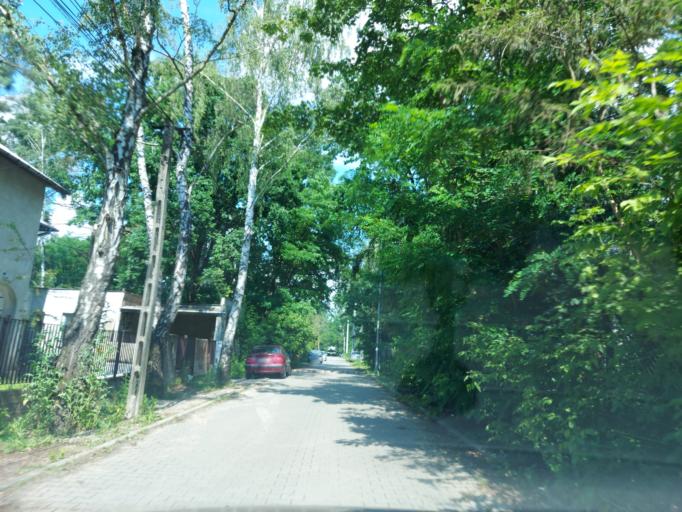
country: PL
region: Masovian Voivodeship
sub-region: Powiat piaseczynski
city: Piaseczno
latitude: 52.0616
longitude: 20.9829
